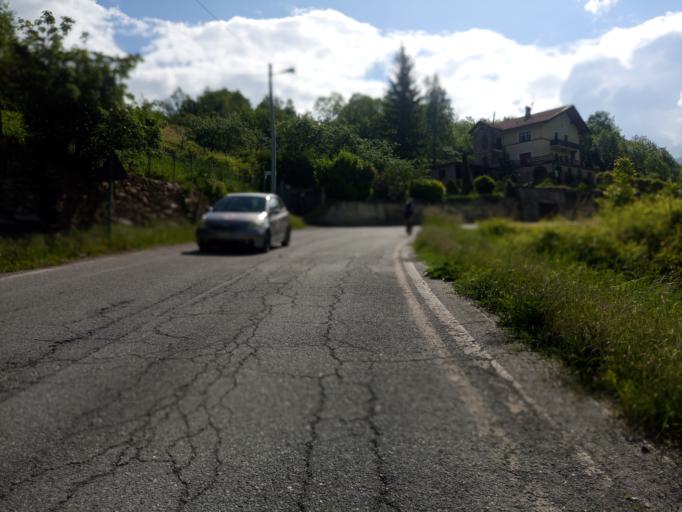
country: IT
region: Piedmont
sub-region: Provincia di Torino
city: Meana di Susa
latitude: 45.1243
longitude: 7.0659
